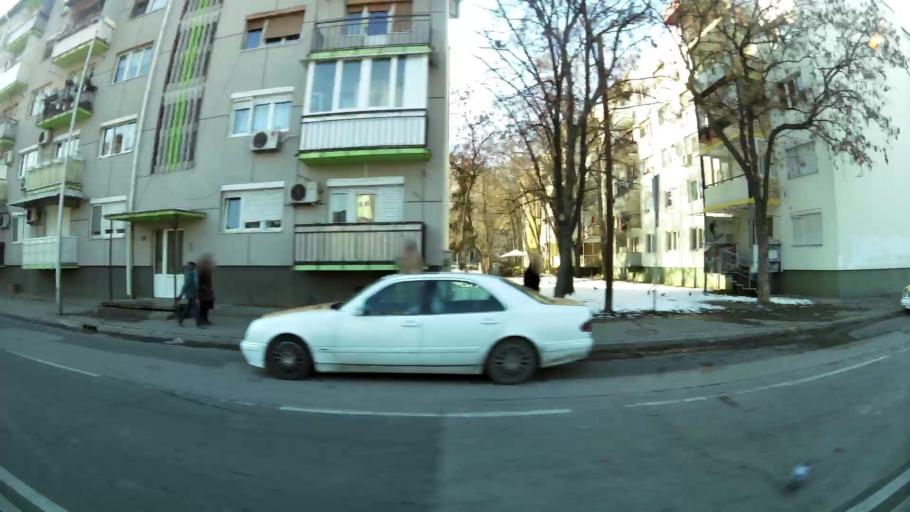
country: MK
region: Karpos
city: Skopje
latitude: 42.0064
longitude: 21.3908
